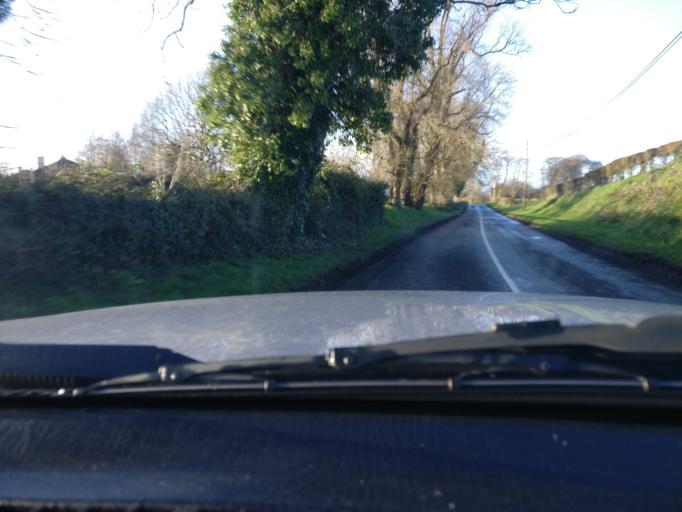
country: IE
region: Leinster
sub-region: An Mhi
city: Athboy
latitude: 53.6942
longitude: -7.0003
